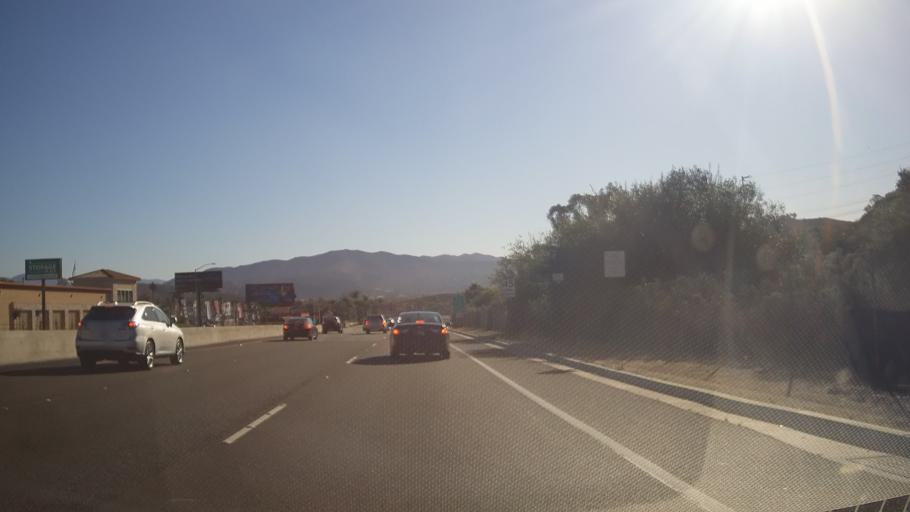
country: US
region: California
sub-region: San Diego County
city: Rancho San Diego
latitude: 32.7393
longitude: -116.9457
